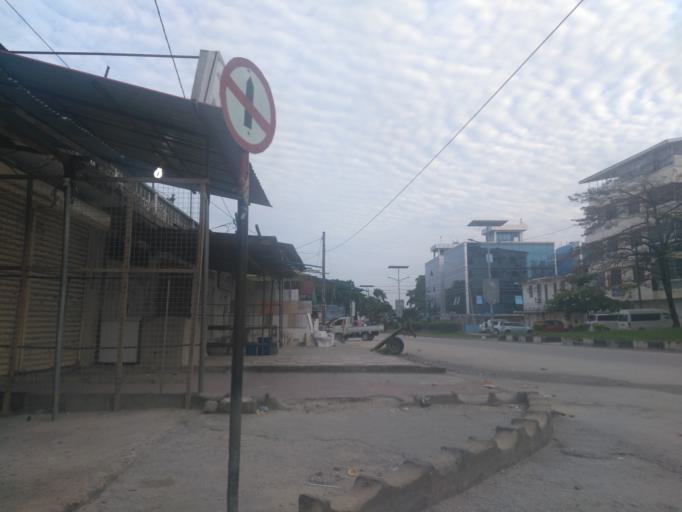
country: TZ
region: Zanzibar Urban/West
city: Zanzibar
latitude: -6.1604
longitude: 39.1986
